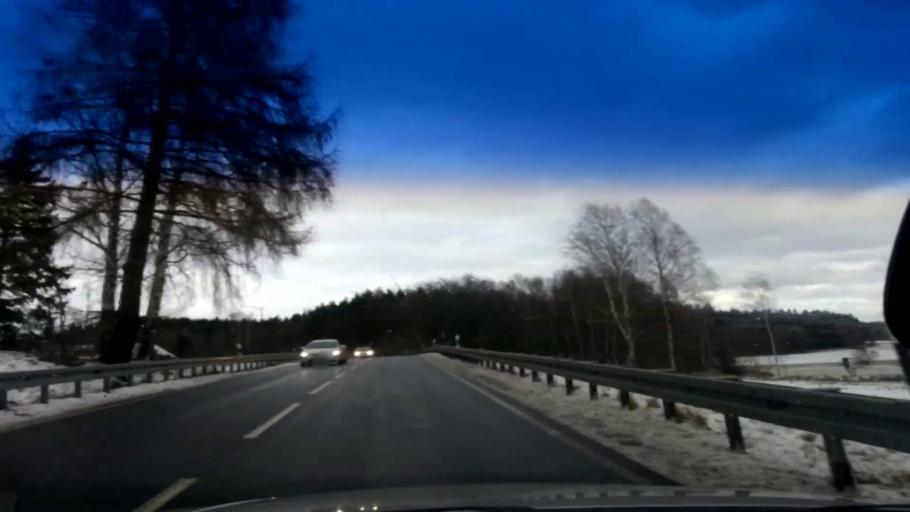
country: DE
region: Bavaria
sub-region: Upper Franconia
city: Marktleuthen
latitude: 50.1409
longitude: 12.0143
